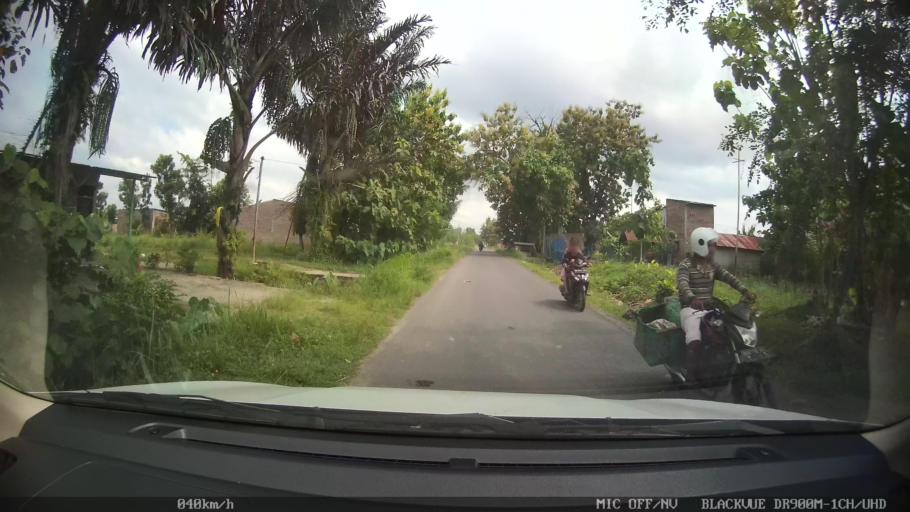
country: ID
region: North Sumatra
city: Sunggal
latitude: 3.6344
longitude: 98.6064
